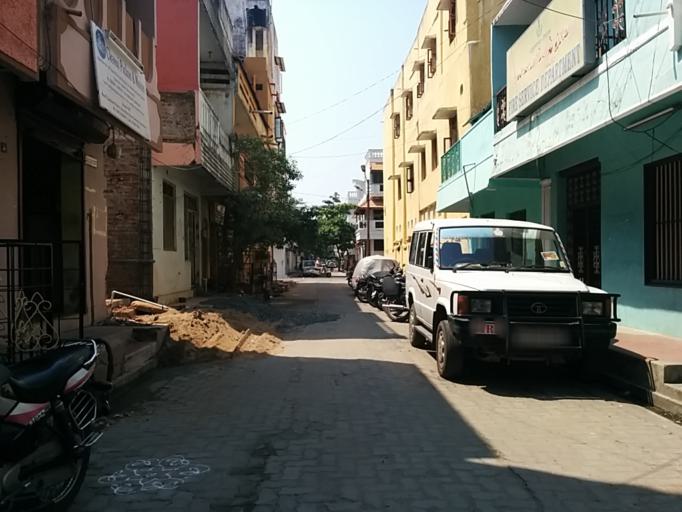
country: IN
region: Pondicherry
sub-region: Puducherry
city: Puducherry
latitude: 11.9379
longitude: 79.8321
